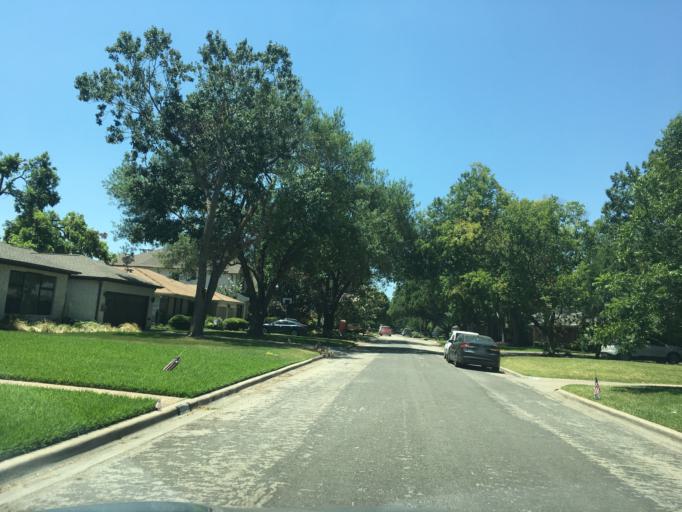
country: US
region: Texas
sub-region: Dallas County
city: Highland Park
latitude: 32.8421
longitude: -96.7405
